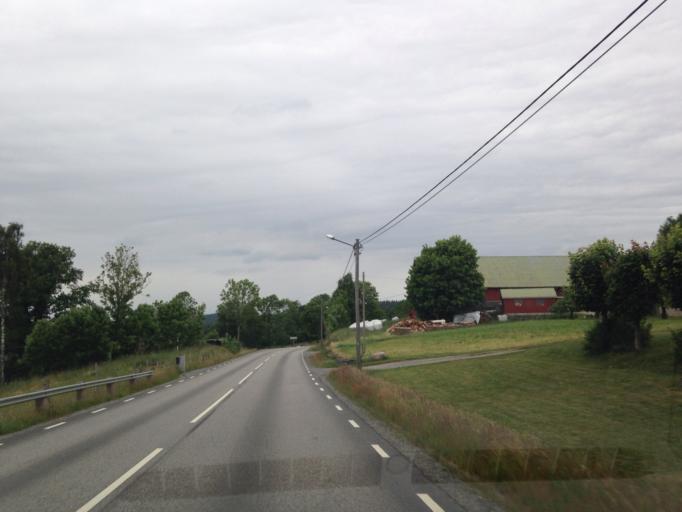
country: SE
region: Vaestra Goetaland
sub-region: Marks Kommun
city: Bua
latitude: 57.5092
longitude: 12.5480
